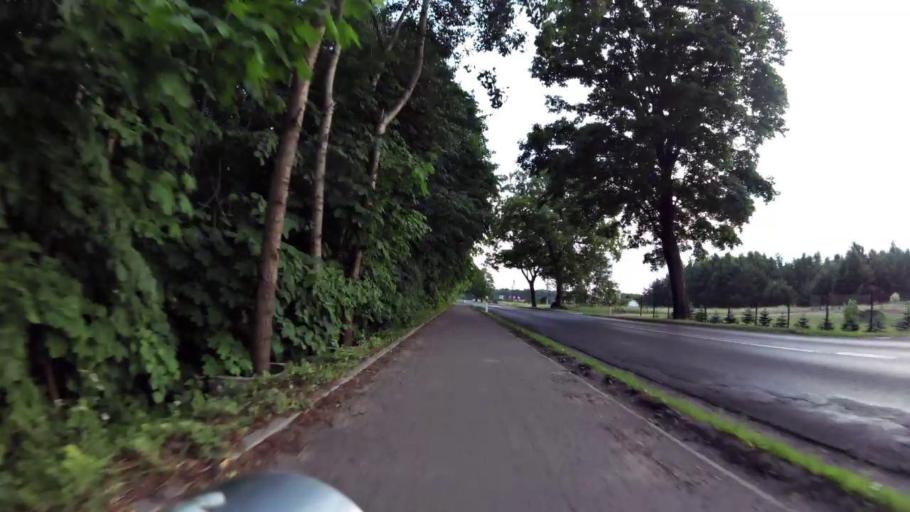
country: PL
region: Kujawsko-Pomorskie
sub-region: Powiat chelminski
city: Unislaw
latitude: 53.1927
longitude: 18.3508
